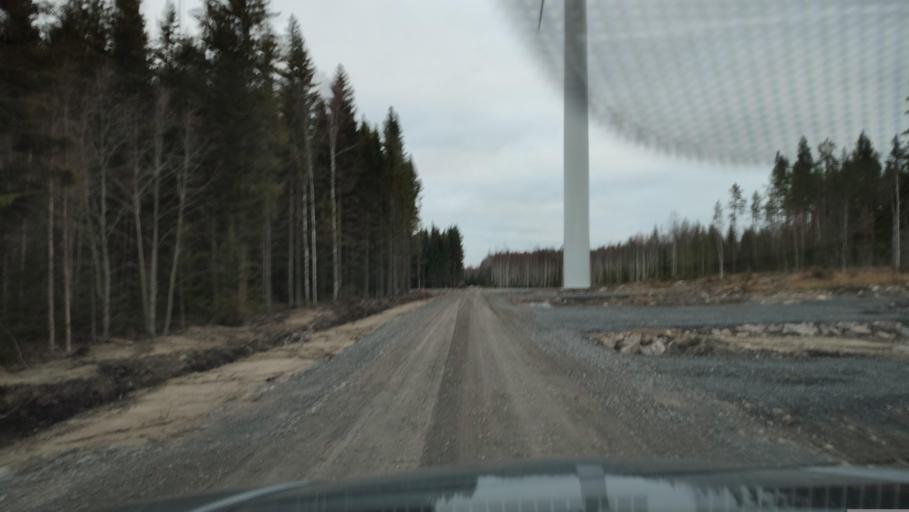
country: FI
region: Southern Ostrobothnia
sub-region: Suupohja
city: Karijoki
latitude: 62.2151
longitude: 21.6018
